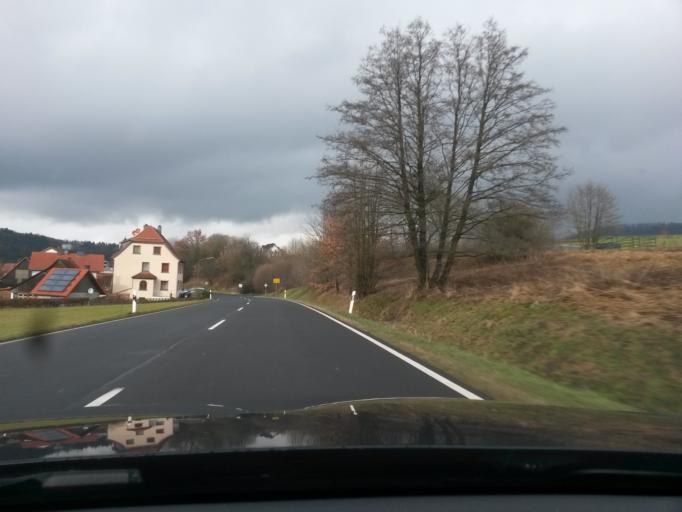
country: DE
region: Thuringia
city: Birx
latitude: 50.5211
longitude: 10.0186
